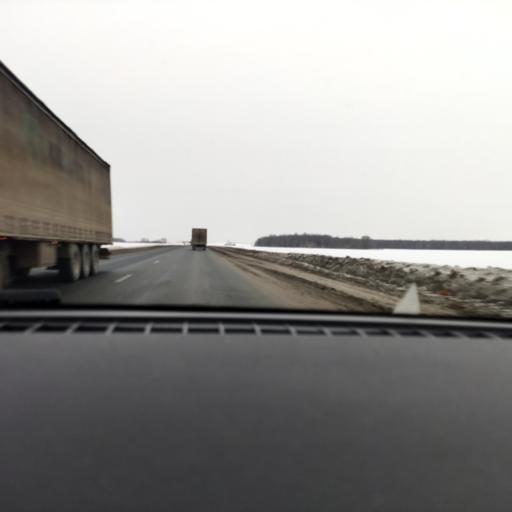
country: RU
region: Samara
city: Petra-Dubrava
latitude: 53.3226
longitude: 50.4552
